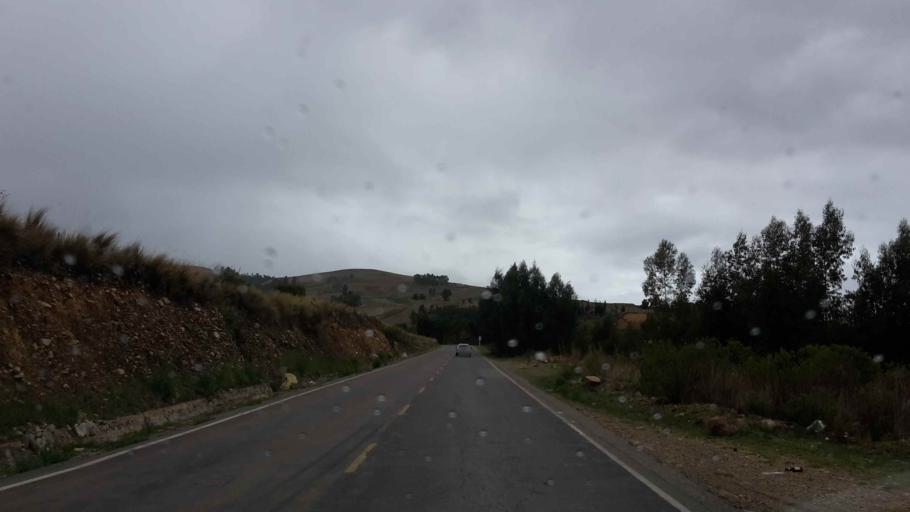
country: BO
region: Cochabamba
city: Arani
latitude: -17.4620
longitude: -65.6807
